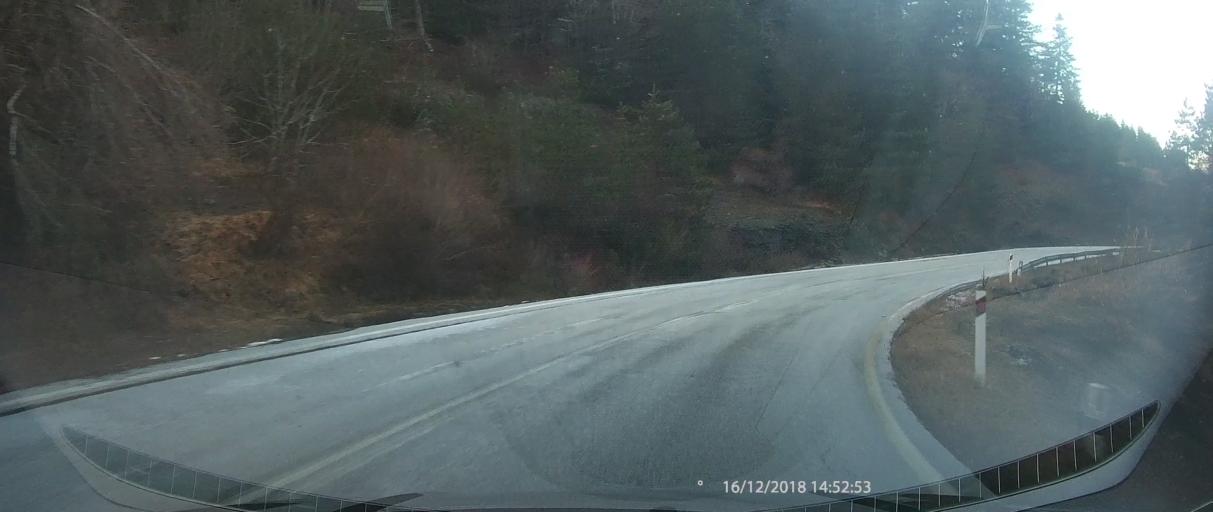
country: GR
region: West Macedonia
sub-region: Nomos Kastorias
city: Nestorio
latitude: 40.2062
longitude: 21.0583
